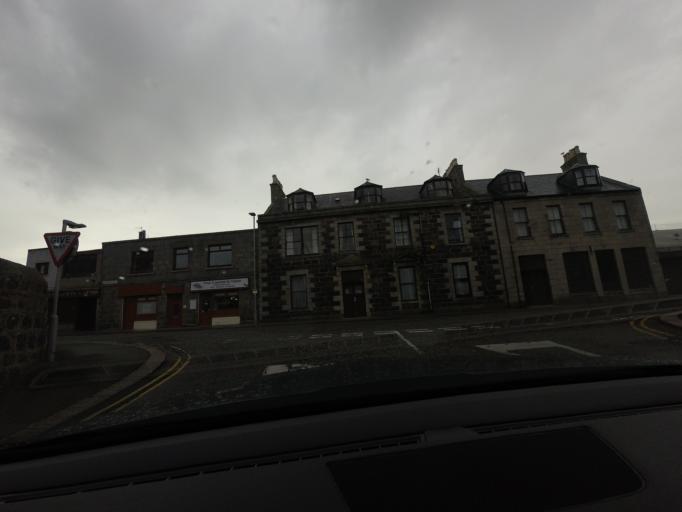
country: GB
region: Scotland
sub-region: Aberdeenshire
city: Fraserburgh
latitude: 57.6904
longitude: -2.0045
